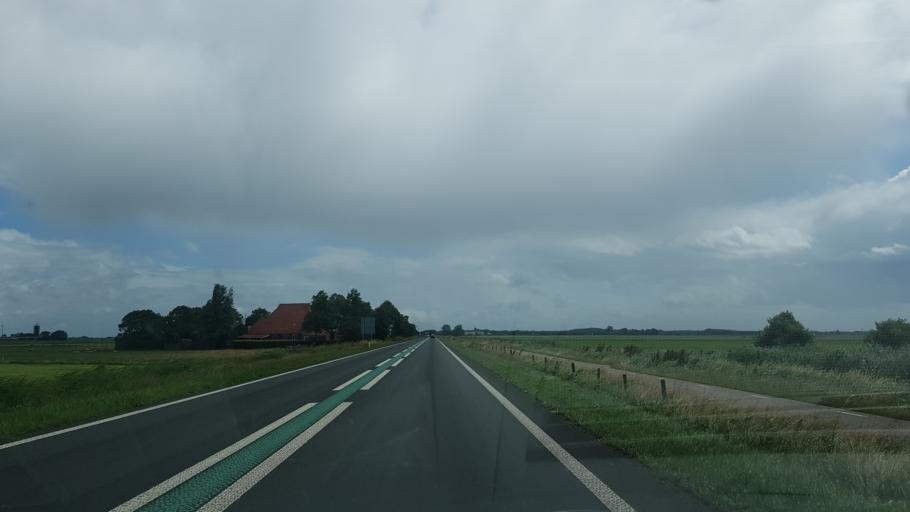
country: NL
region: Friesland
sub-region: Gemeente Ferwerderadiel
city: Burdaard
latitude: 53.2842
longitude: 5.9108
